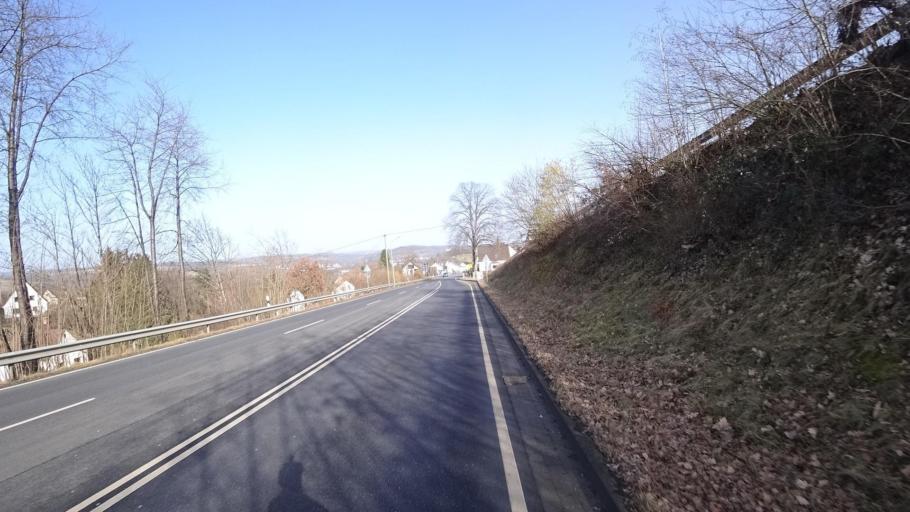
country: DE
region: Rheinland-Pfalz
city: Bruchertseifen
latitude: 50.7656
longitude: 7.7097
